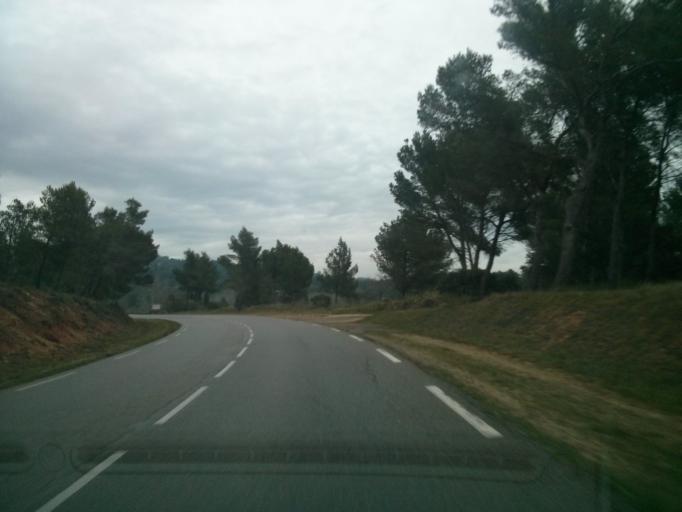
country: FR
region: Provence-Alpes-Cote d'Azur
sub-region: Departement des Bouches-du-Rhone
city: Paradou
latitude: 43.7292
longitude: 4.7724
